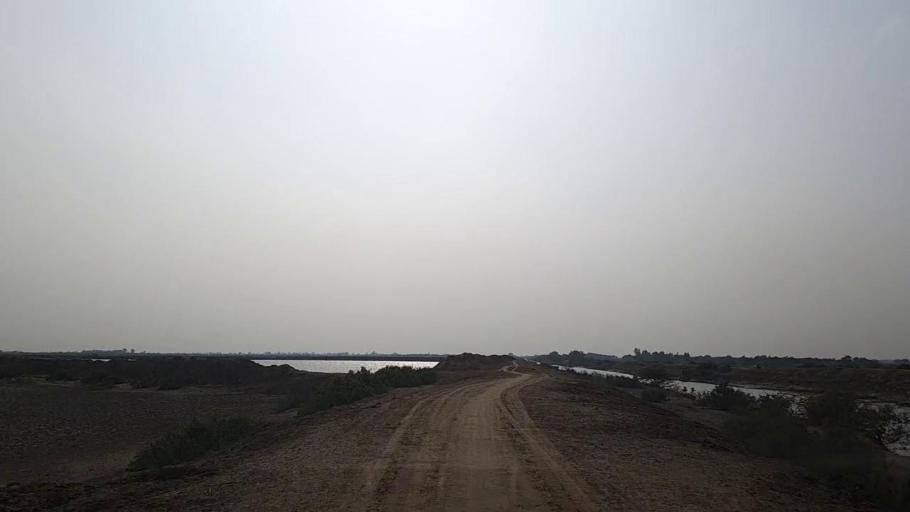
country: PK
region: Sindh
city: Gharo
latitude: 24.6673
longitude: 67.6356
